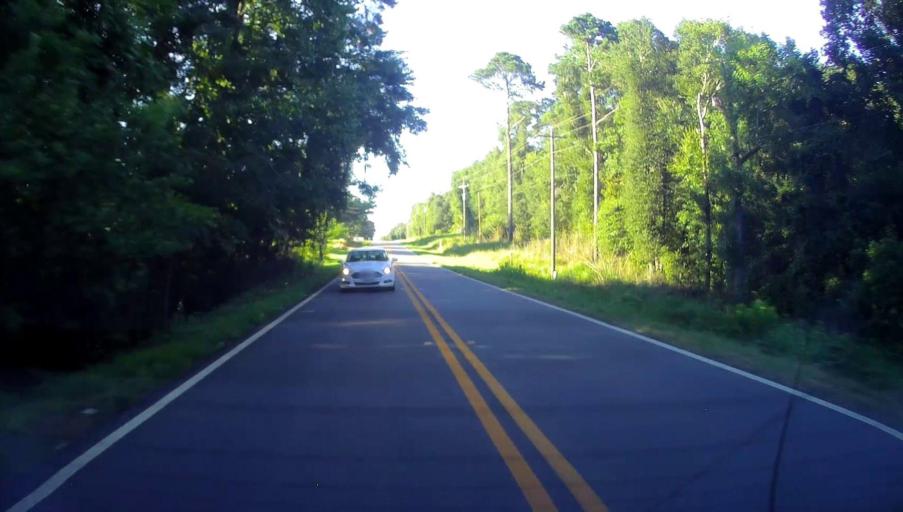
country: US
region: Georgia
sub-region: Pulaski County
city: Hawkinsville
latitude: 32.2878
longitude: -83.4489
